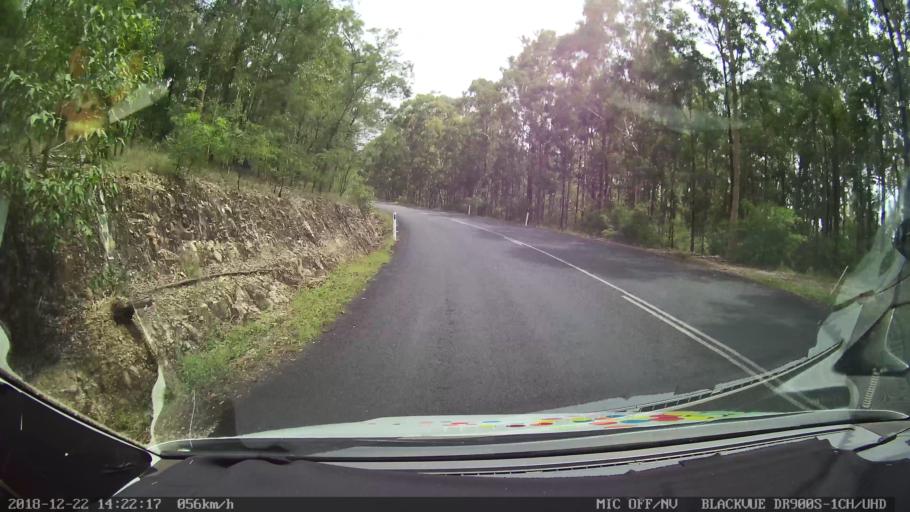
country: AU
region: New South Wales
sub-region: Clarence Valley
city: Coutts Crossing
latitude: -30.0247
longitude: 152.6539
